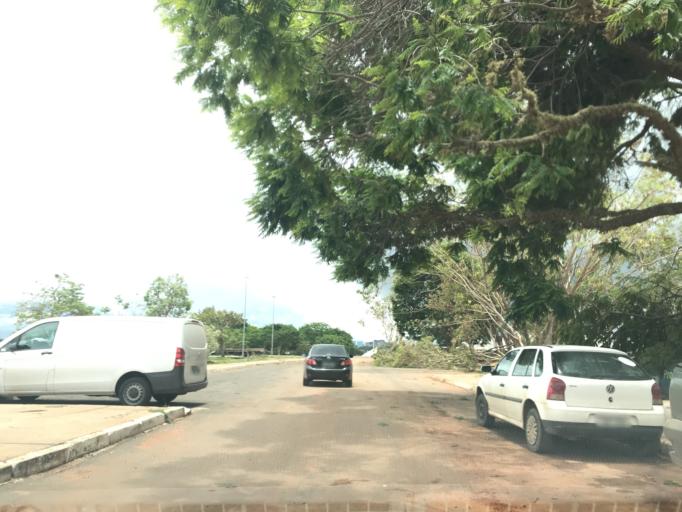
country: BR
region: Federal District
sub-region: Brasilia
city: Brasilia
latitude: -15.7867
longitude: -47.8339
